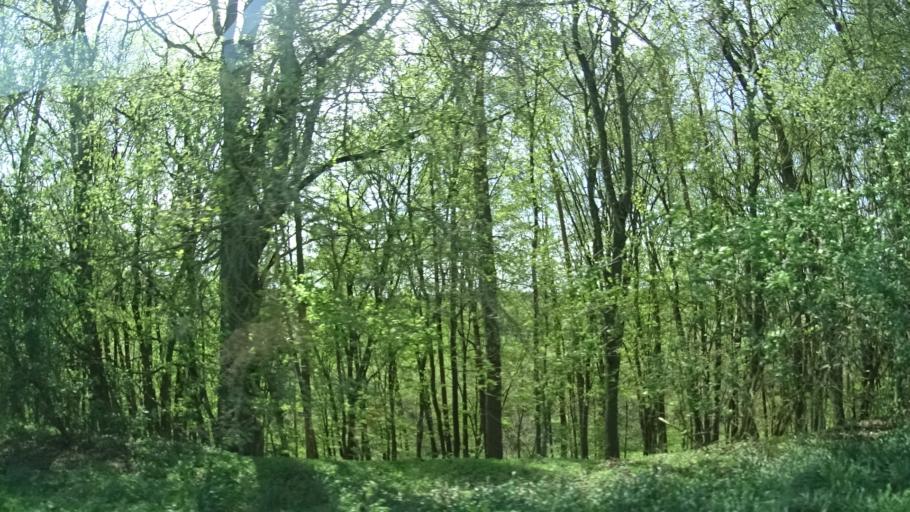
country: DE
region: Bavaria
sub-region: Regierungsbezirk Unterfranken
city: Burgpreppach
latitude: 50.1534
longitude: 10.5990
